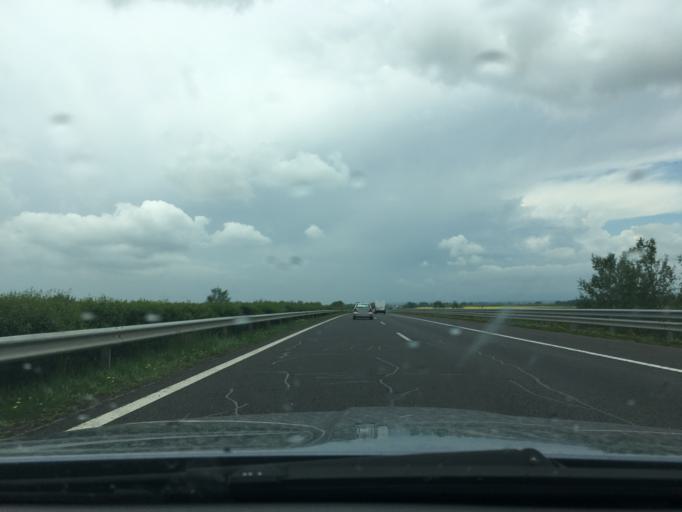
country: HU
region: Borsod-Abauj-Zemplen
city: Hejobaba
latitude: 47.8760
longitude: 20.9214
